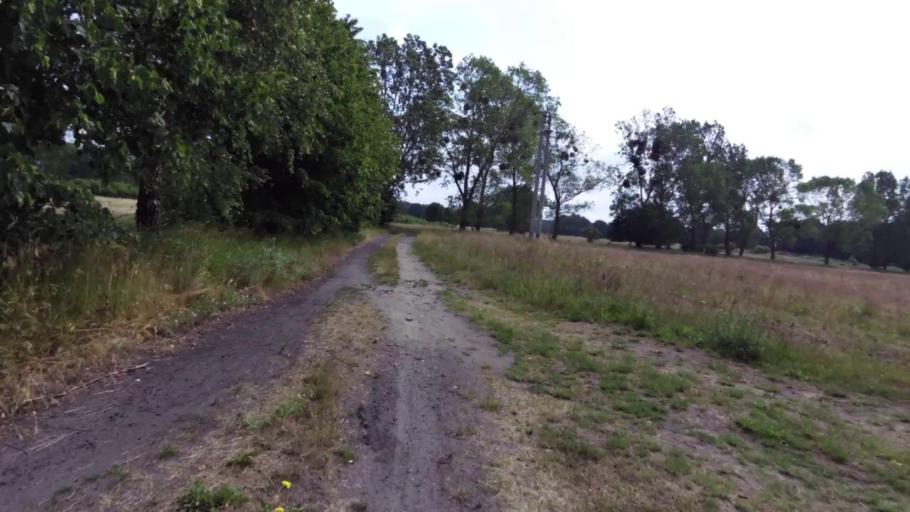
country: PL
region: West Pomeranian Voivodeship
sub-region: Powiat kamienski
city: Wolin
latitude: 53.7578
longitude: 14.6510
